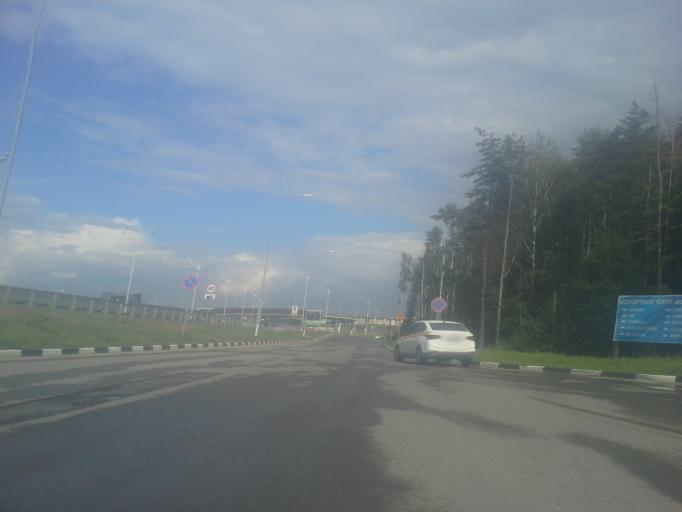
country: RU
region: Moskovskaya
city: Lesnoy Gorodok
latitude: 55.6260
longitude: 37.1947
